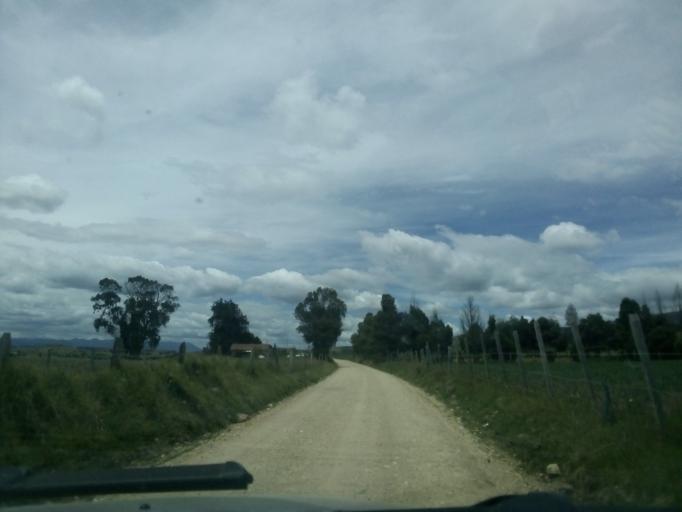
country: CO
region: Boyaca
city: Toca
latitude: 5.6124
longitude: -73.1471
